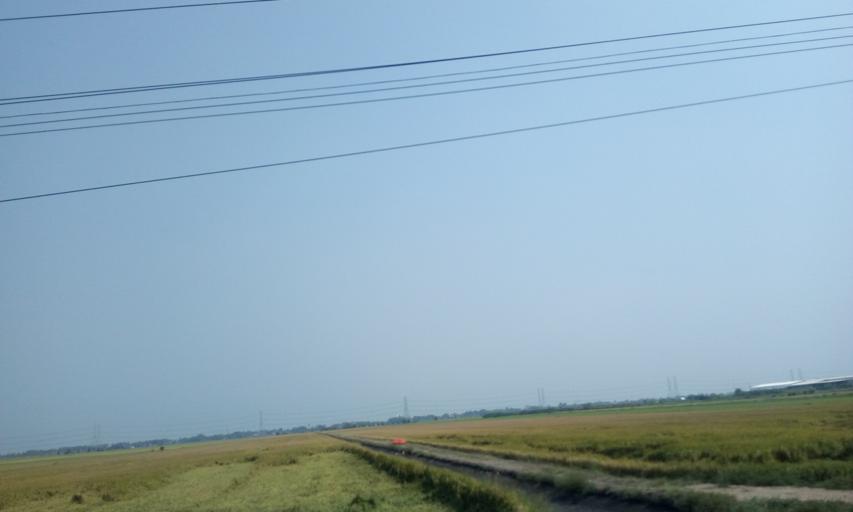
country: TH
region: Pathum Thani
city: Ban Lam Luk Ka
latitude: 13.9871
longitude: 100.7558
